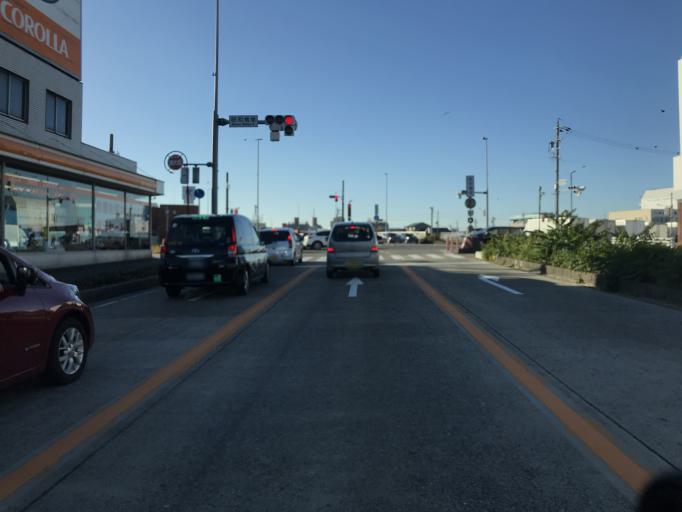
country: JP
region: Aichi
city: Nagoya-shi
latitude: 35.1251
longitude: 136.8781
